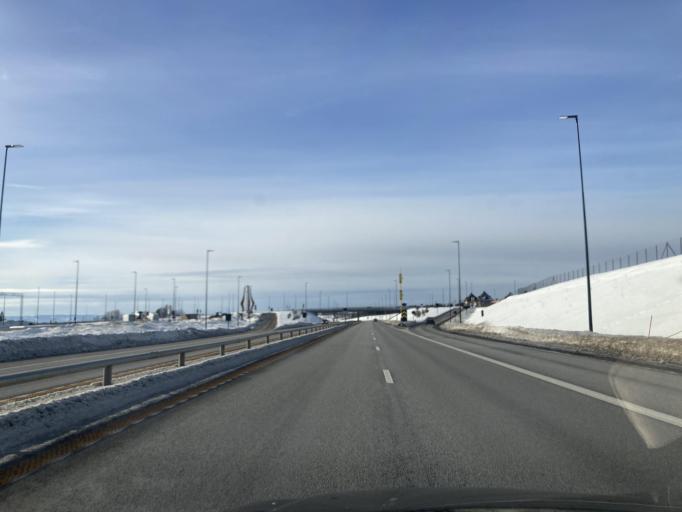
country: NO
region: Hedmark
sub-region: Loten
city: Loten
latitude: 60.8501
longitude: 11.3757
